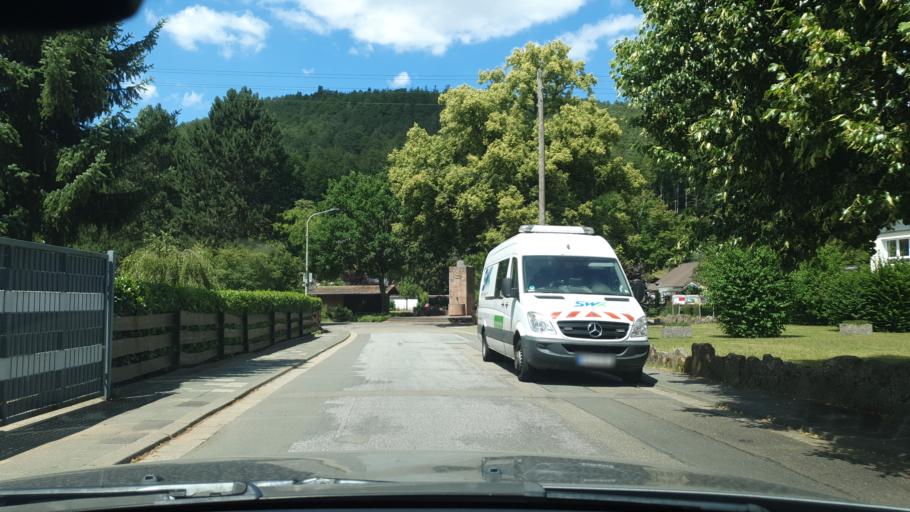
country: DE
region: Rheinland-Pfalz
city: Trippstadt
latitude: 49.3793
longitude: 7.8210
